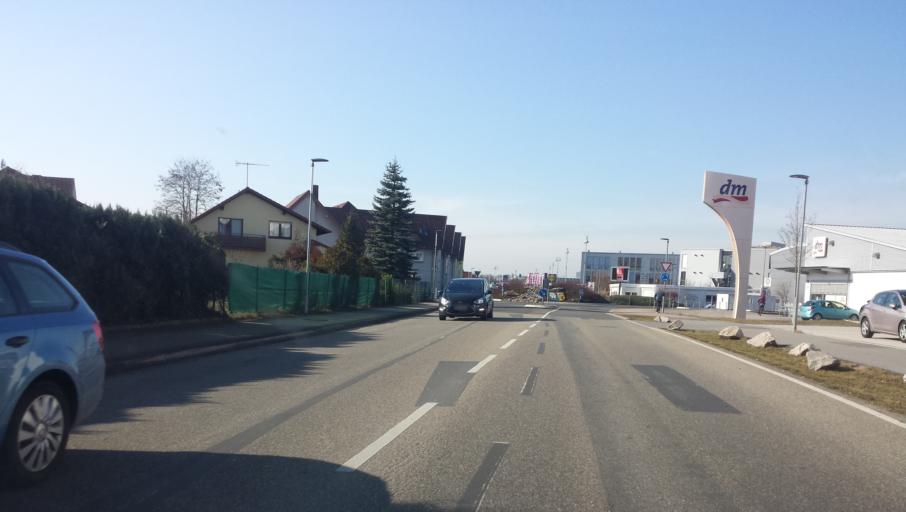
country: DE
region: Baden-Wuerttemberg
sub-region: Karlsruhe Region
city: Sankt Leon-Rot
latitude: 49.2670
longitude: 8.6193
